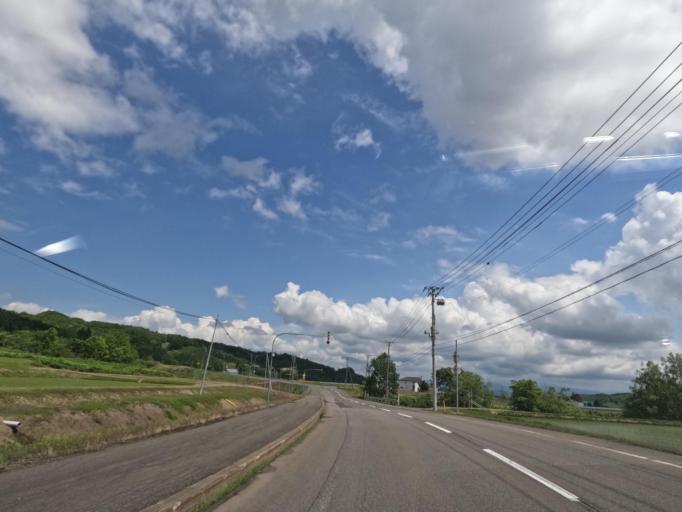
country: JP
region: Hokkaido
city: Takikawa
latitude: 43.5810
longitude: 141.8203
